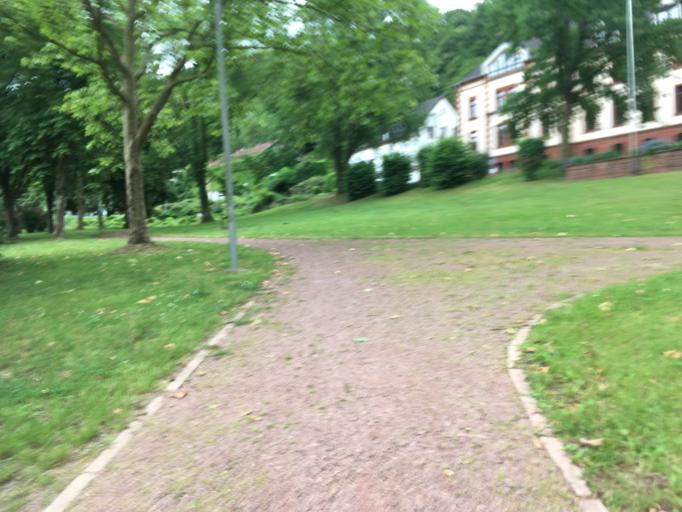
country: DE
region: Saarland
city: Mettlach
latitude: 49.4910
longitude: 6.5944
